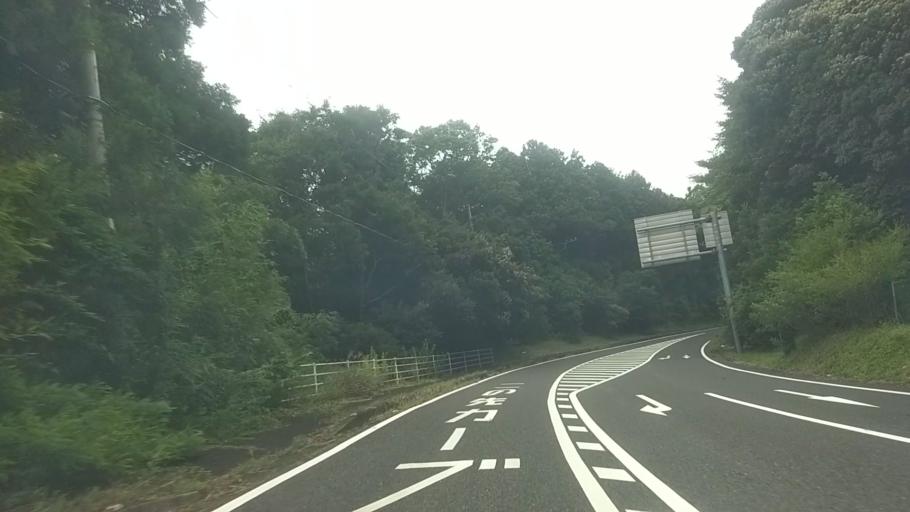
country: JP
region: Chiba
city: Kawaguchi
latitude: 35.2241
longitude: 140.0214
